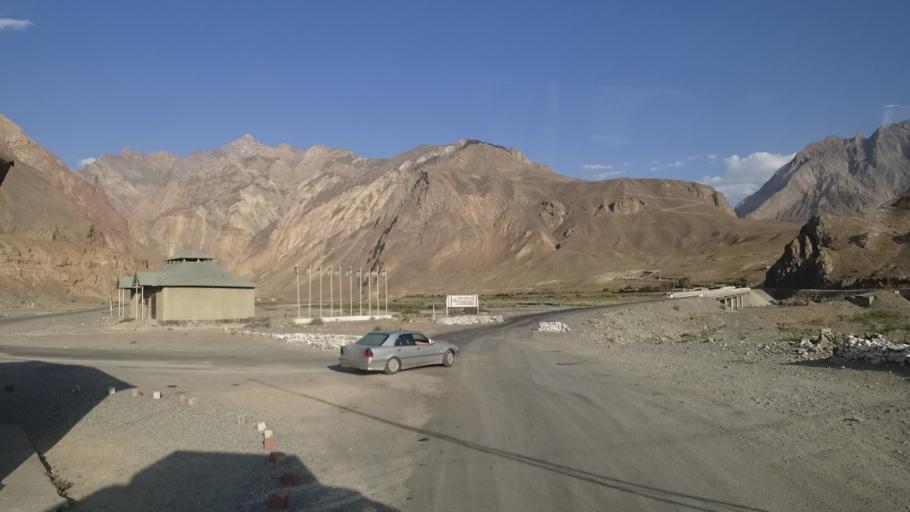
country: TJ
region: Gorno-Badakhshan
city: Vanj
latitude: 38.2999
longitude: 71.3365
